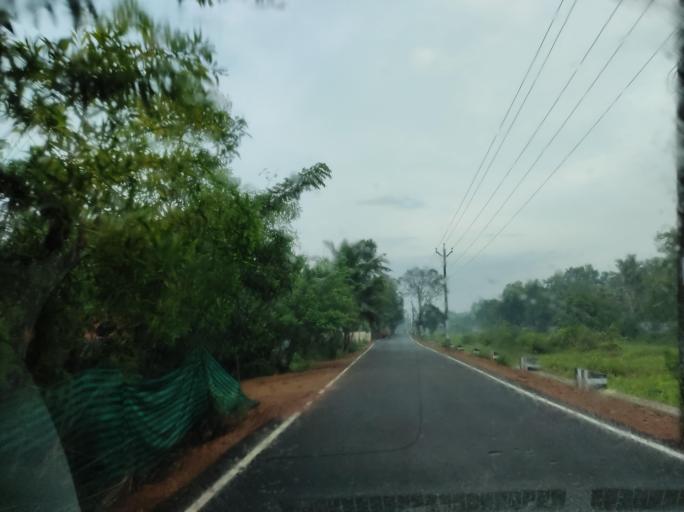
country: IN
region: Kerala
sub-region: Alappuzha
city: Shertallai
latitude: 9.5930
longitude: 76.3331
